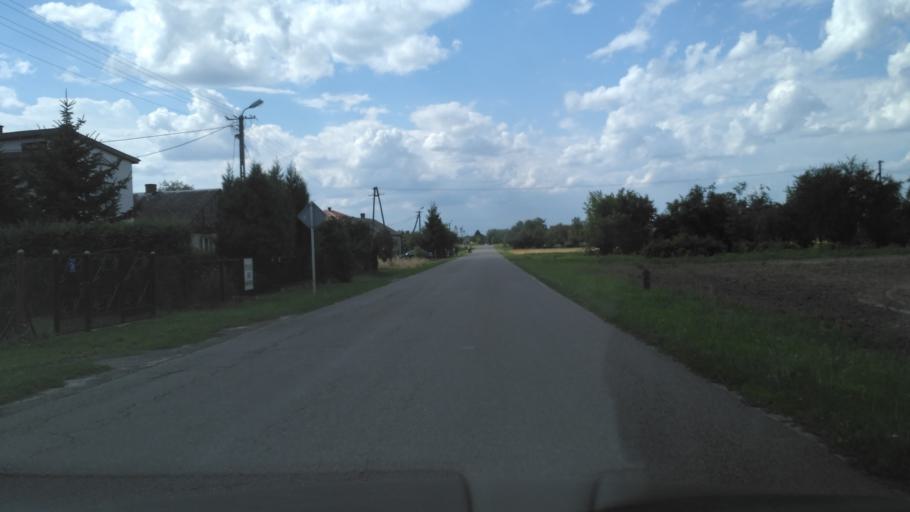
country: PL
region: Lublin Voivodeship
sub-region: Powiat swidnicki
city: Trawniki
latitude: 51.1771
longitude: 22.9673
